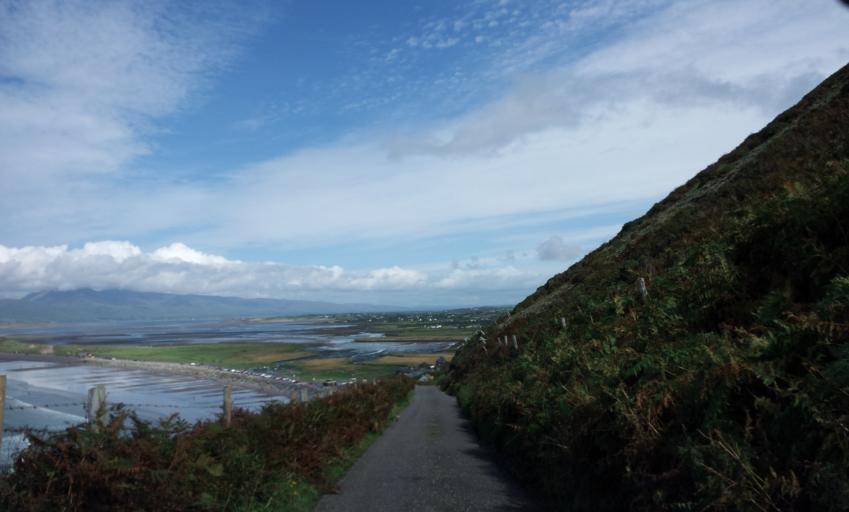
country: IE
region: Munster
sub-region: Ciarrai
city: Killorglin
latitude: 52.0508
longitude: -9.9820
